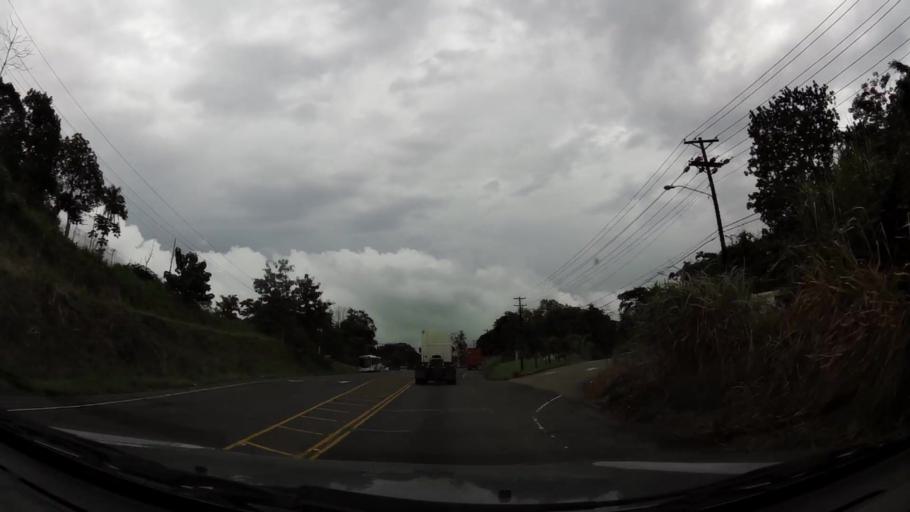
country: PA
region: Colon
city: Nuevo Vigia
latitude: 9.2214
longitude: -79.6264
